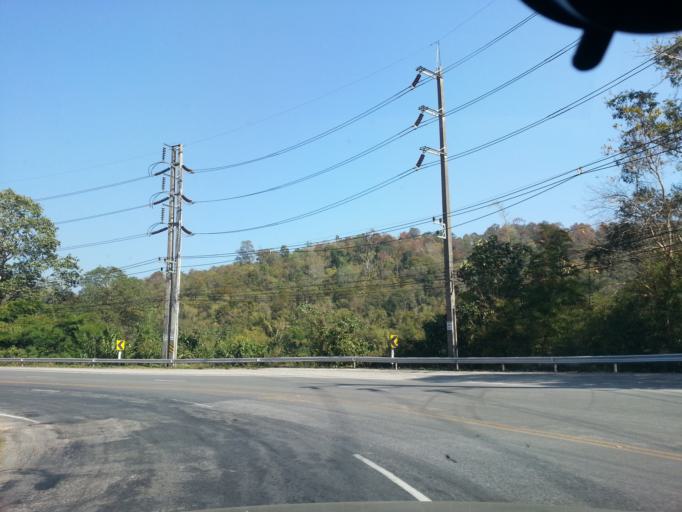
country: TH
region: Chiang Mai
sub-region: Amphoe Chiang Dao
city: Chiang Dao
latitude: 19.2516
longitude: 98.9716
